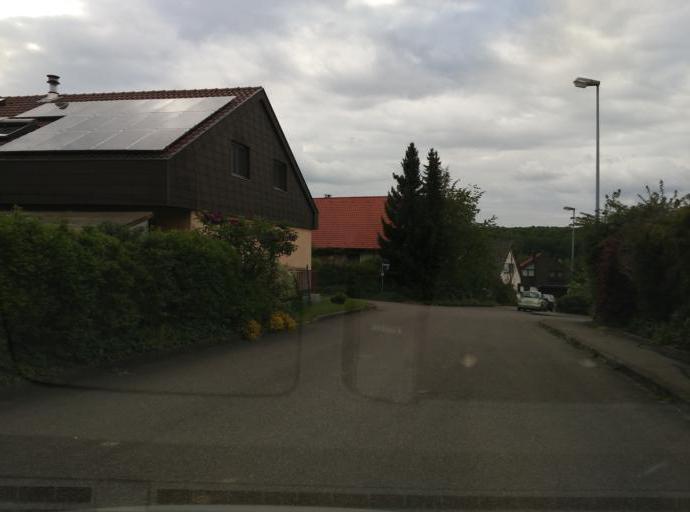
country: DE
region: Baden-Wuerttemberg
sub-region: Regierungsbezirk Stuttgart
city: Frickenhausen
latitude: 48.5881
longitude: 9.3547
